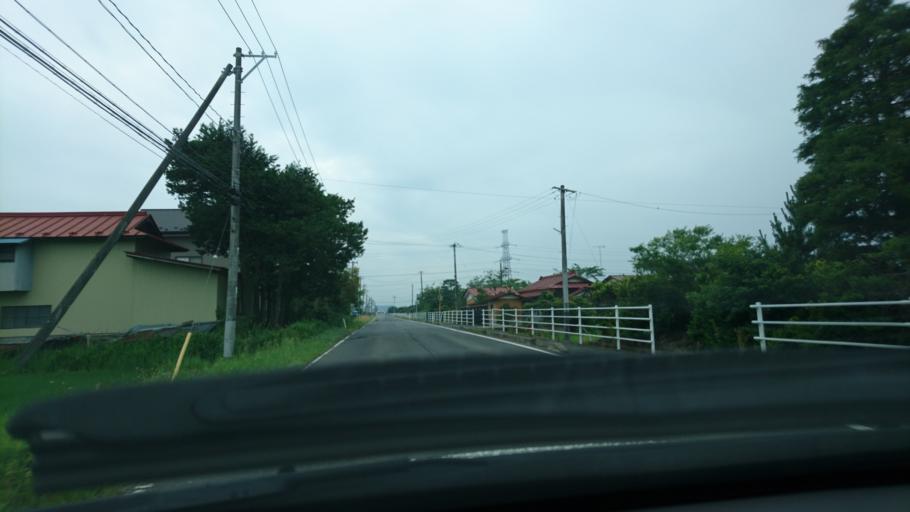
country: JP
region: Miyagi
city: Furukawa
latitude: 38.7309
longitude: 140.9774
